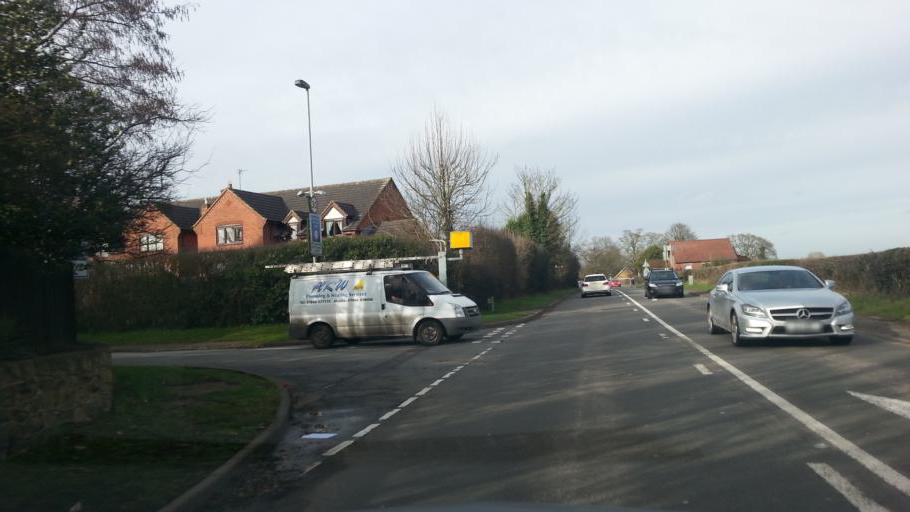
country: GB
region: England
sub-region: Staffordshire
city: Colwich
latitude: 52.8378
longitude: -2.0321
